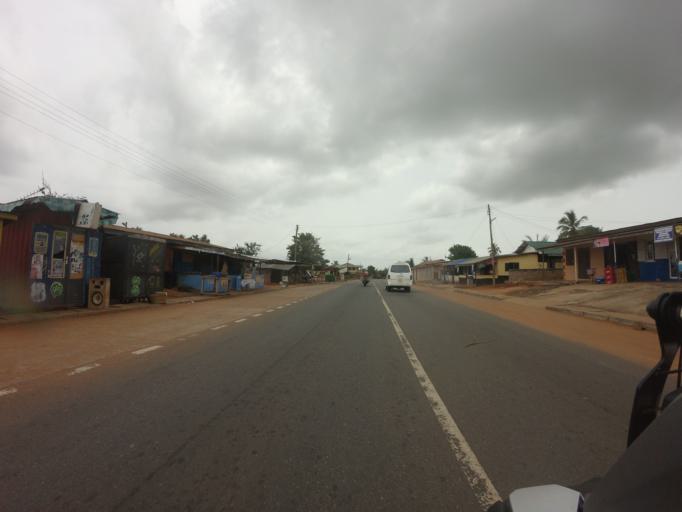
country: GH
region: Volta
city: Keta
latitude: 6.0644
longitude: 0.9166
